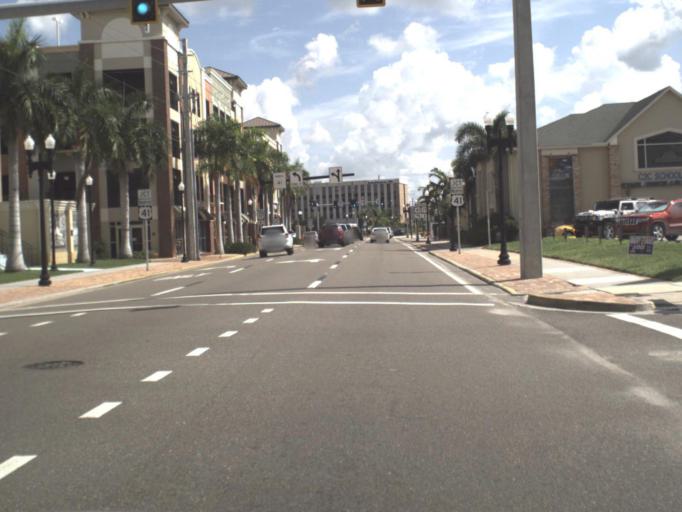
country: US
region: Florida
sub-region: Charlotte County
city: Punta Gorda
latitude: 26.9342
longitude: -82.0502
